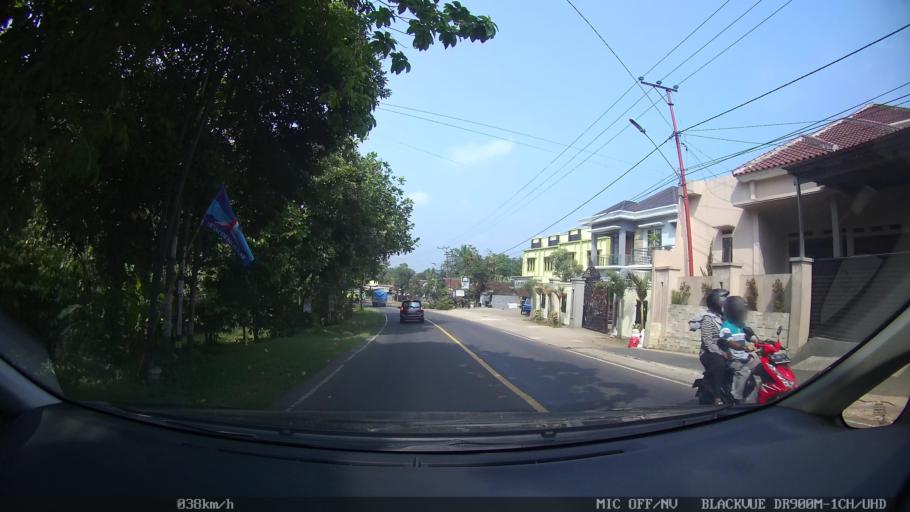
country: ID
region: Lampung
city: Gedongtataan
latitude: -5.3710
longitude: 105.1313
